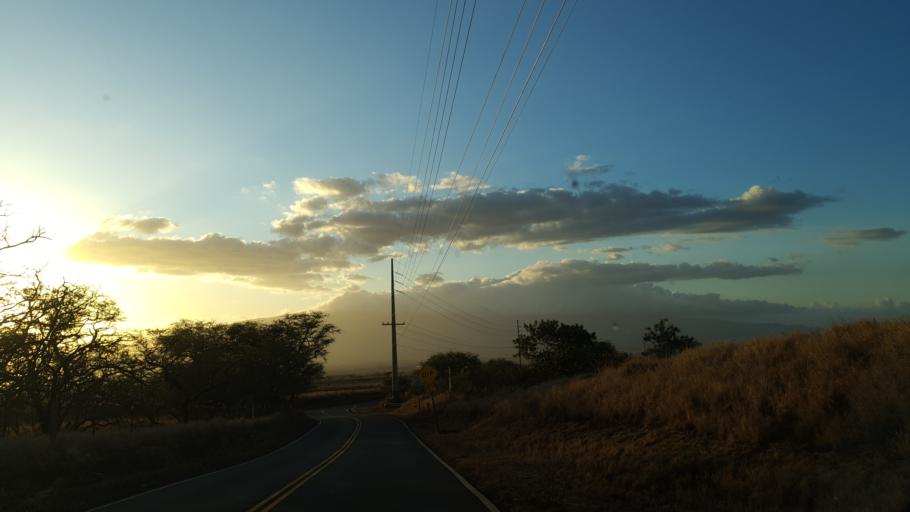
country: US
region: Hawaii
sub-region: Maui County
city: Pukalani
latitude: 20.7958
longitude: -156.3685
